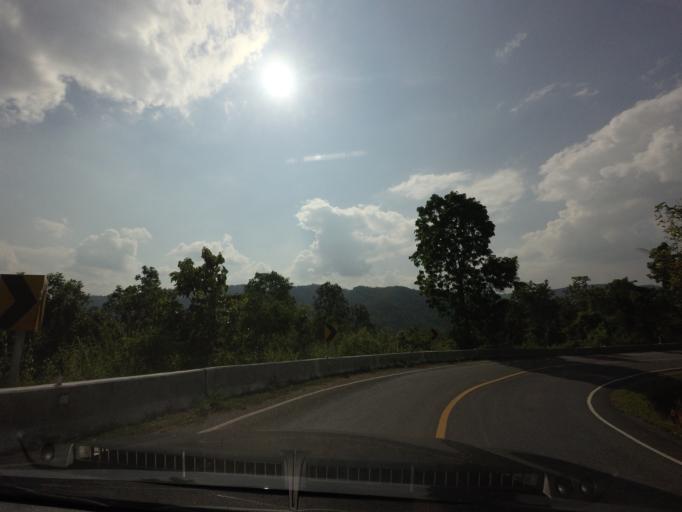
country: TH
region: Uttaradit
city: Ban Khok
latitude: 18.2487
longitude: 100.9984
